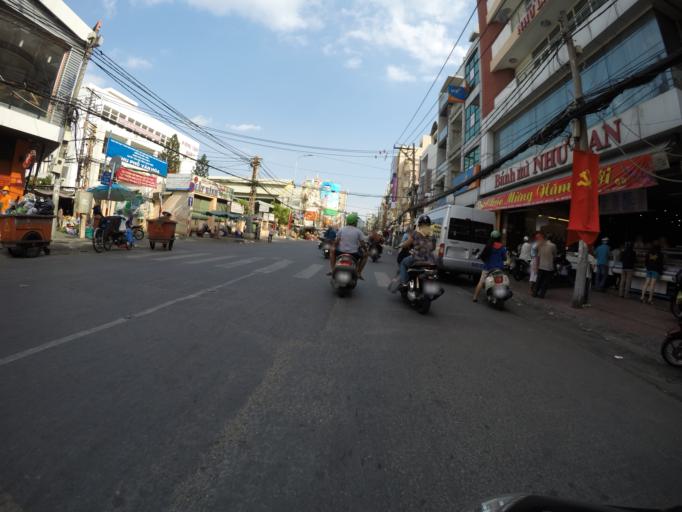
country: VN
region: Ho Chi Minh City
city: Quan Mot
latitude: 10.7899
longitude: 106.6892
